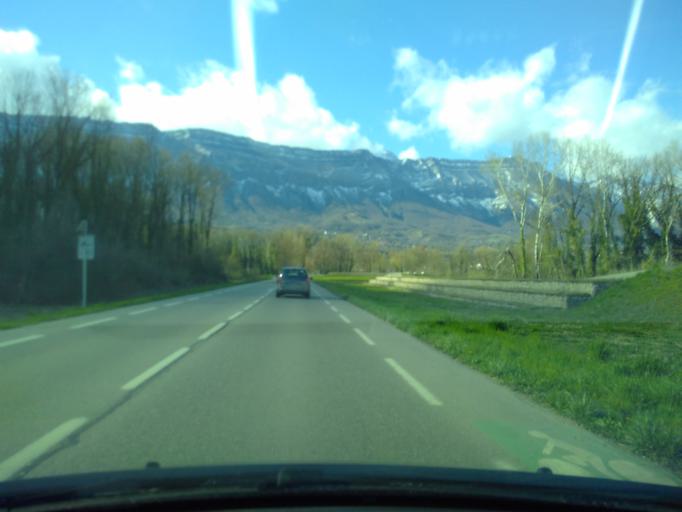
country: FR
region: Rhone-Alpes
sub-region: Departement de l'Isere
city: Domene
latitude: 45.2161
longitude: 5.8245
